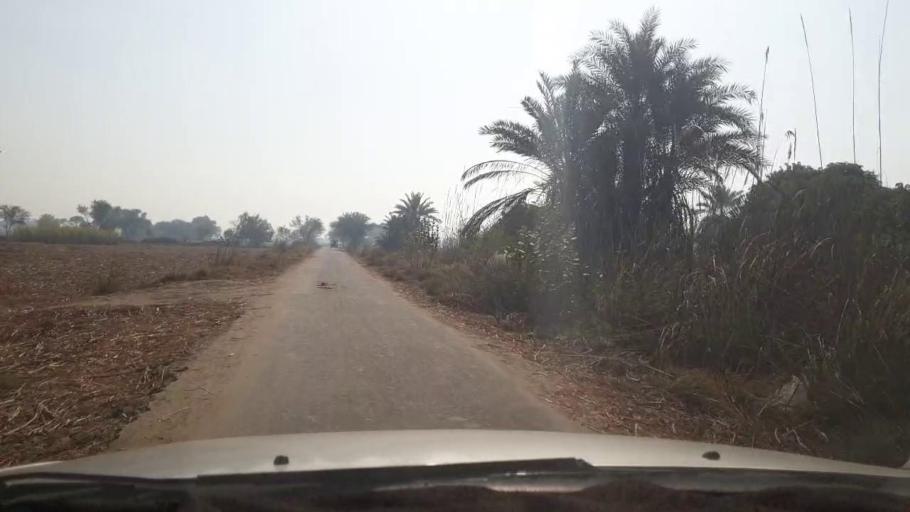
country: PK
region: Sindh
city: Khanpur
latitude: 27.7452
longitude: 69.5035
